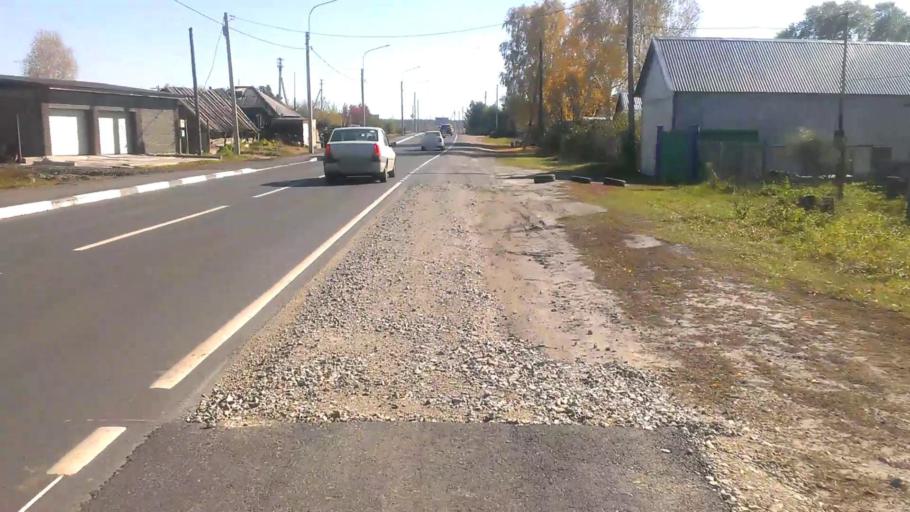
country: RU
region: Altai Krai
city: Sannikovo
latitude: 53.3159
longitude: 83.9588
